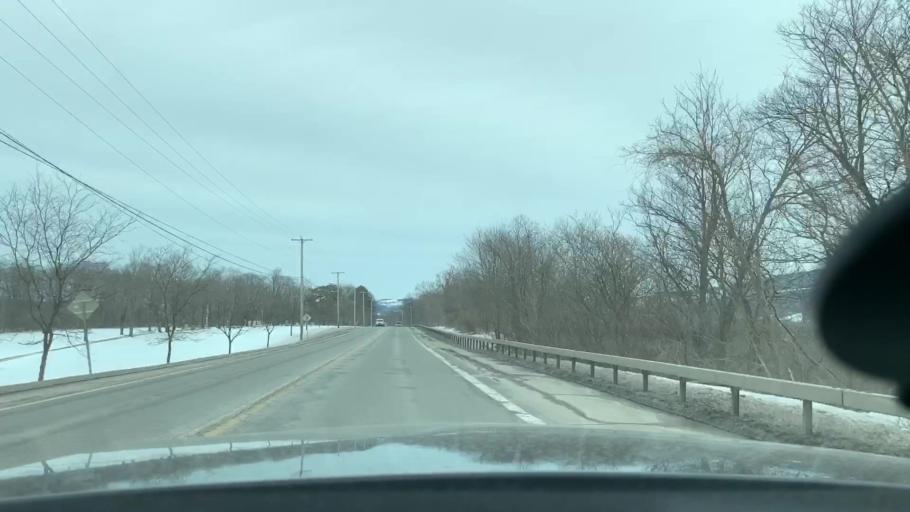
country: US
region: New York
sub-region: Herkimer County
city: Herkimer
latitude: 43.0256
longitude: -74.9417
